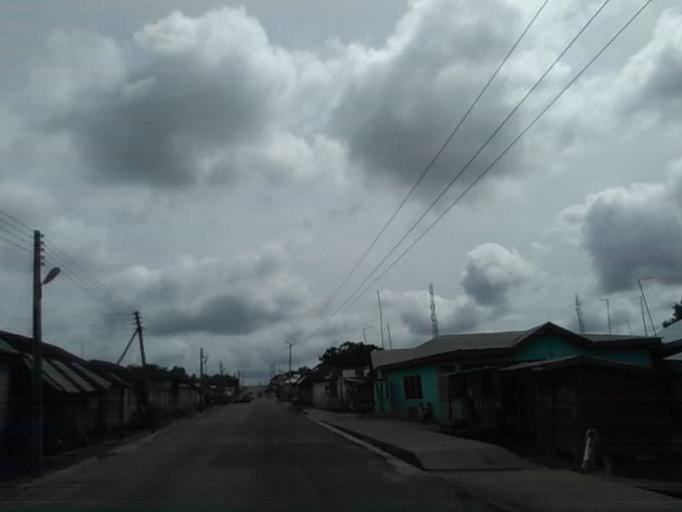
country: GH
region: Ashanti
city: Mamponteng
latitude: 6.7491
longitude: -1.4562
